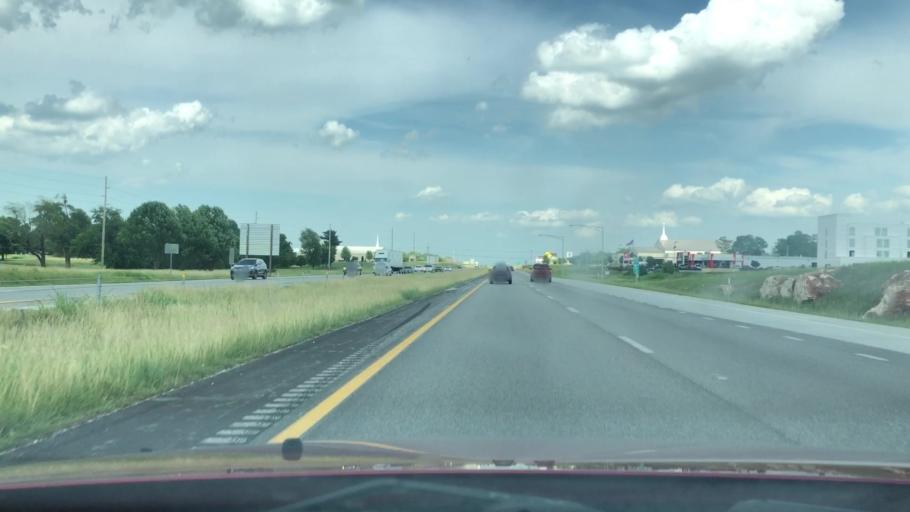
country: US
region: Missouri
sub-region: Greene County
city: Springfield
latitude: 37.2502
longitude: -93.2565
